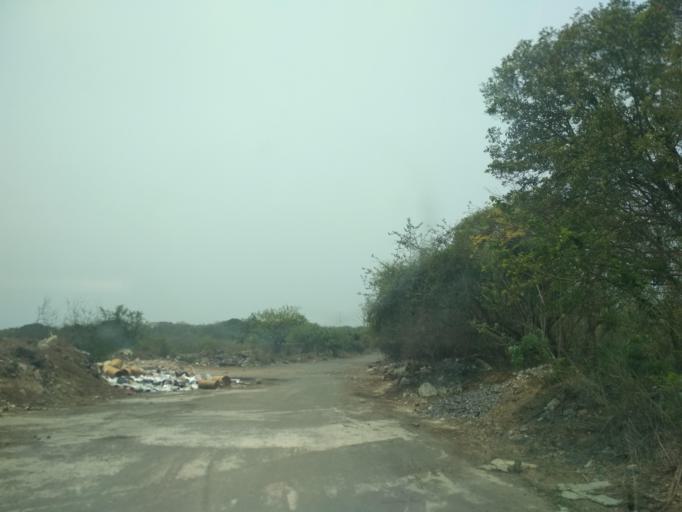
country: MX
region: Veracruz
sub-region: Veracruz
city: Oasis
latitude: 19.1902
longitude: -96.2459
